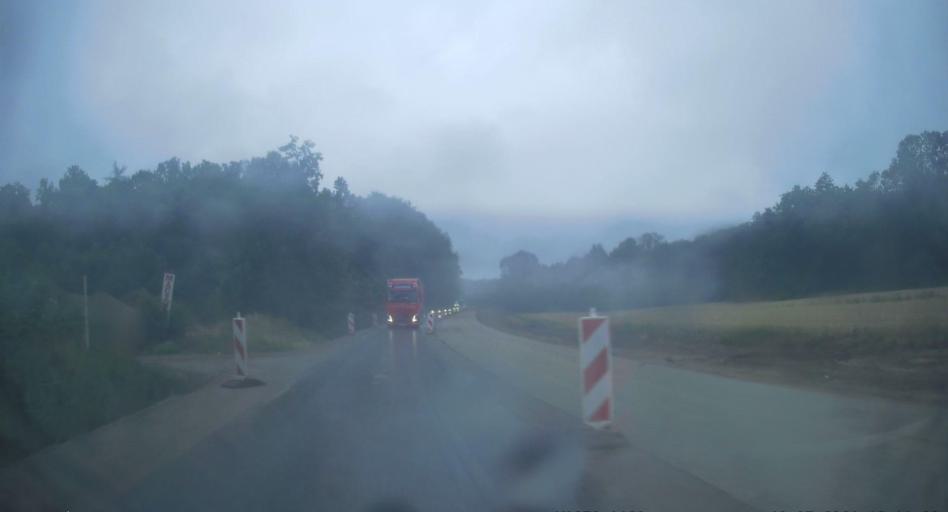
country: PL
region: Opole Voivodeship
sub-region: Powiat nyski
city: Nysa
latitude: 50.4392
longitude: 17.4064
